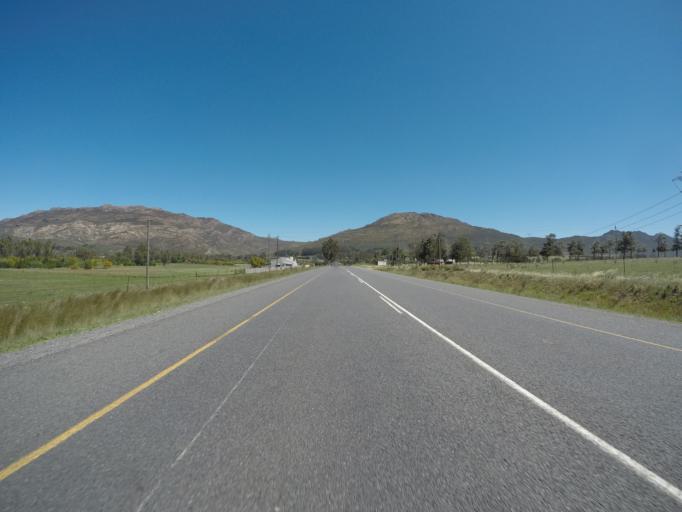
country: ZA
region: Western Cape
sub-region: Cape Winelands District Municipality
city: Ceres
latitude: -33.3089
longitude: 19.1068
